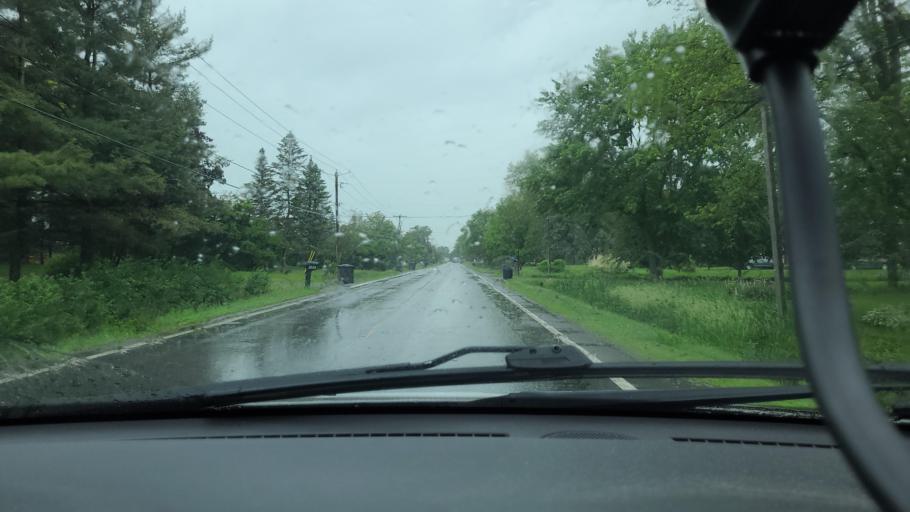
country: CA
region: Quebec
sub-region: Monteregie
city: Saint-Hyacinthe
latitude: 45.6162
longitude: -73.0388
